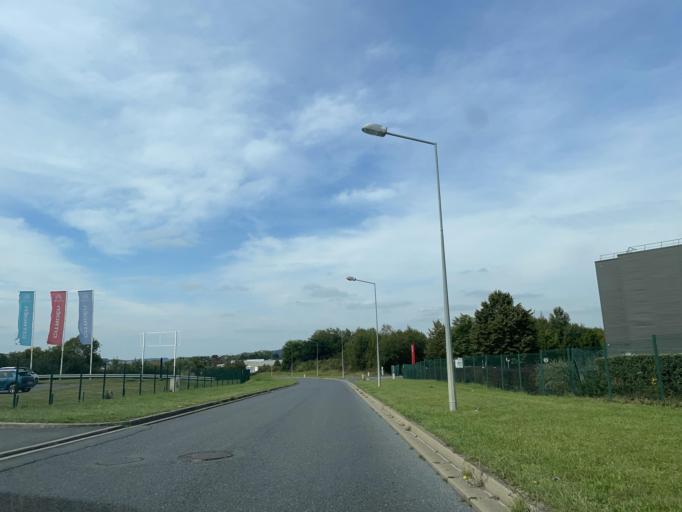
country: FR
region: Ile-de-France
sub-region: Departement de Seine-et-Marne
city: Coulommiers
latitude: 48.8045
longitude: 3.0996
